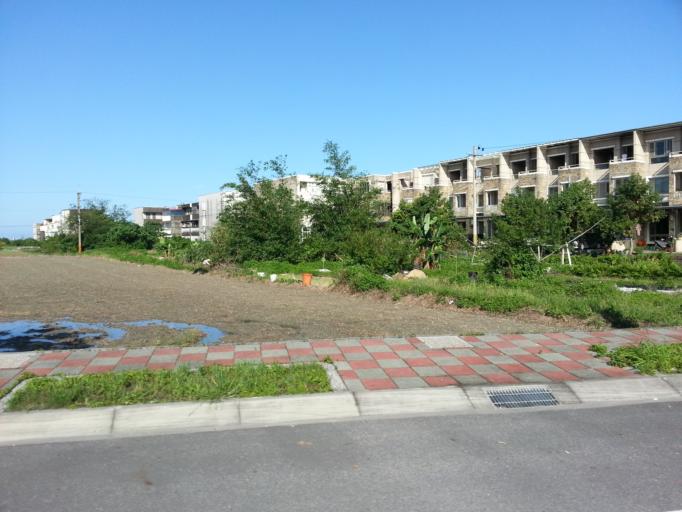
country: TW
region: Taiwan
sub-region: Yilan
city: Yilan
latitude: 24.6187
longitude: 121.8310
